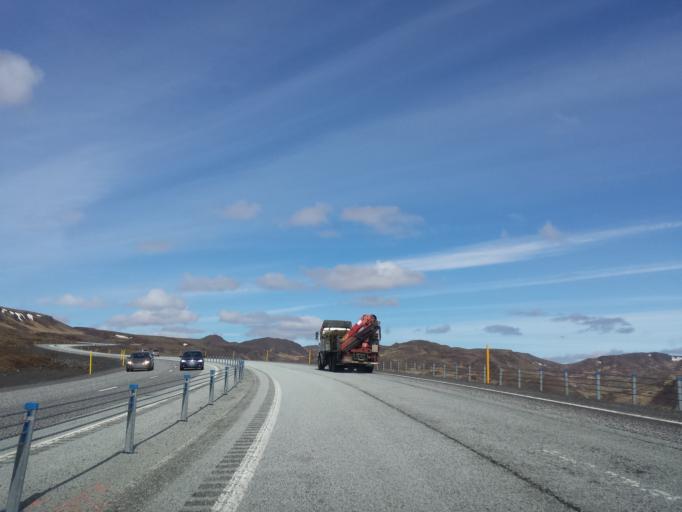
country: IS
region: South
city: Hveragerdi
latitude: 64.0070
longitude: -21.2171
